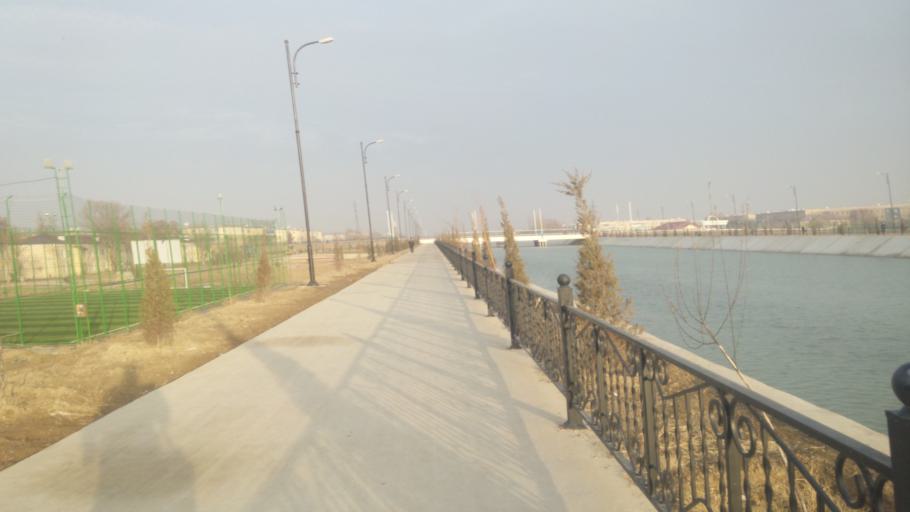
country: UZ
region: Sirdaryo
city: Guliston
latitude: 40.5089
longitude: 68.7784
